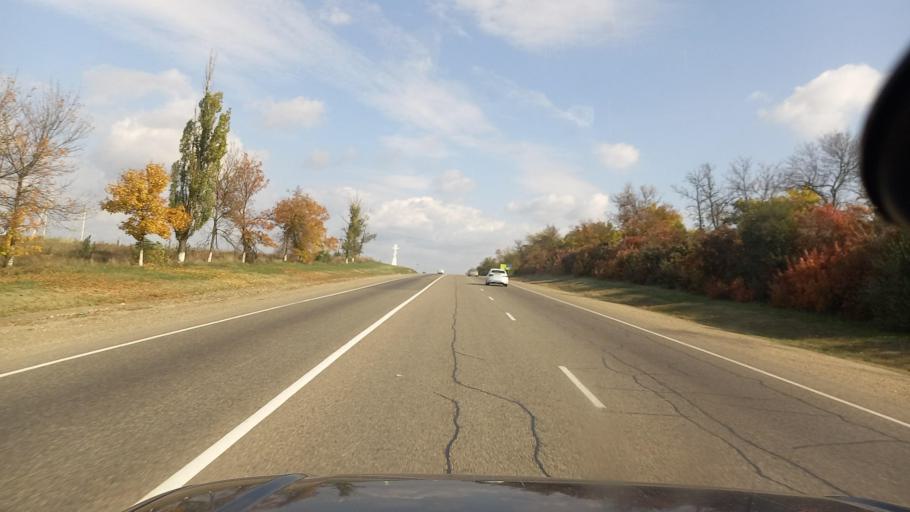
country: RU
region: Krasnodarskiy
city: Akhtyrskiy
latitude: 44.8466
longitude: 38.3125
